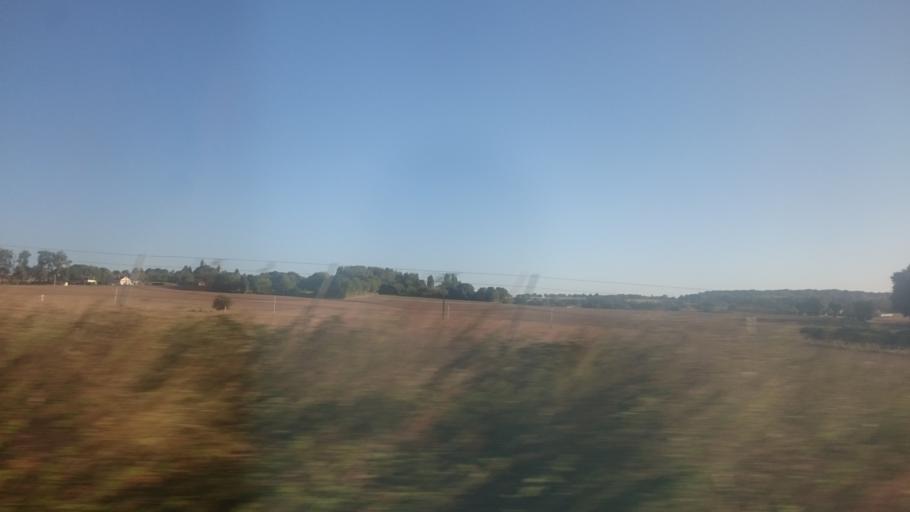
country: FR
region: Centre
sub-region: Departement d'Eure-et-Loir
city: La Bazoche-Gouet
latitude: 48.0843
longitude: 0.9163
